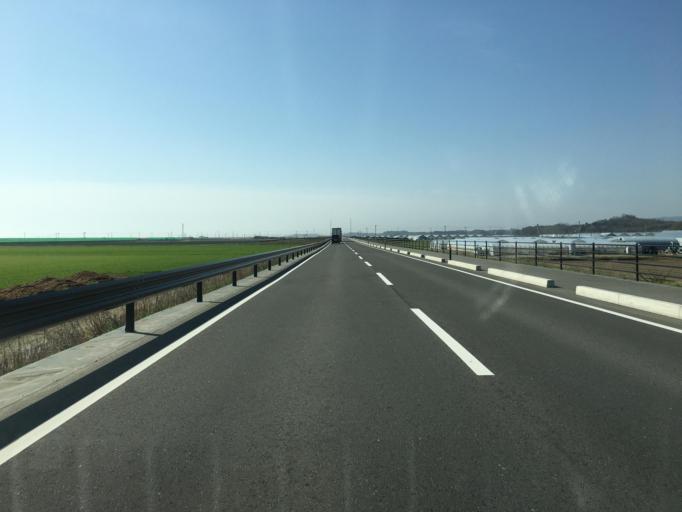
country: JP
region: Miyagi
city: Watari
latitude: 37.9532
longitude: 140.9052
